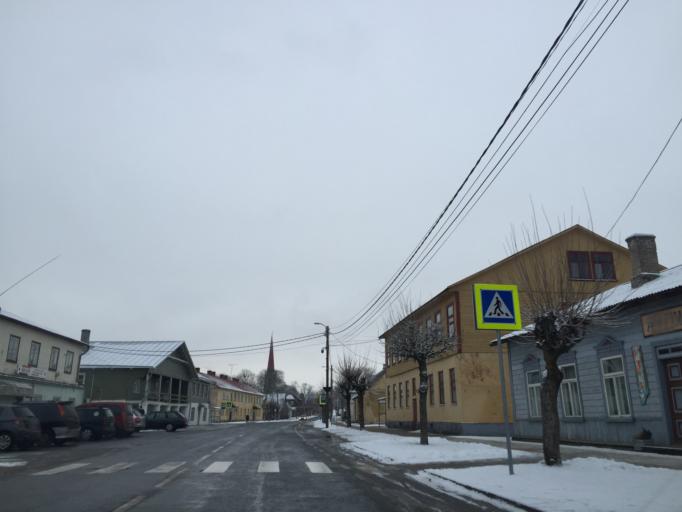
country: EE
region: Laeaene
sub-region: Lihula vald
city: Lihula
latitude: 58.6883
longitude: 23.8349
